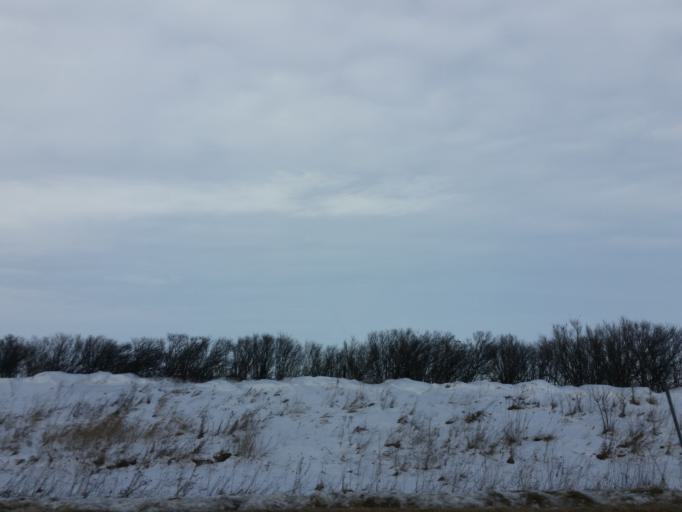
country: US
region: Iowa
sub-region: Delaware County
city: Manchester
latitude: 42.4646
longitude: -91.6041
